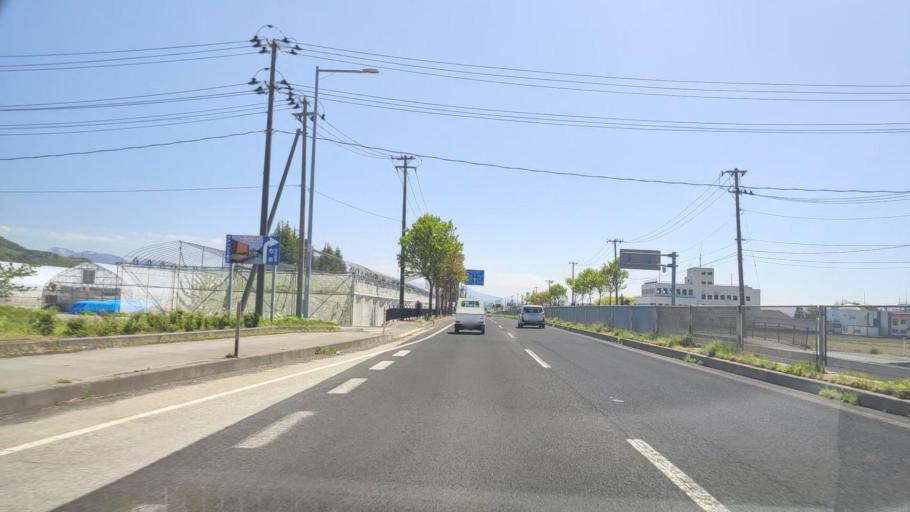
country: JP
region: Yamagata
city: Higashine
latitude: 38.4862
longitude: 140.3831
